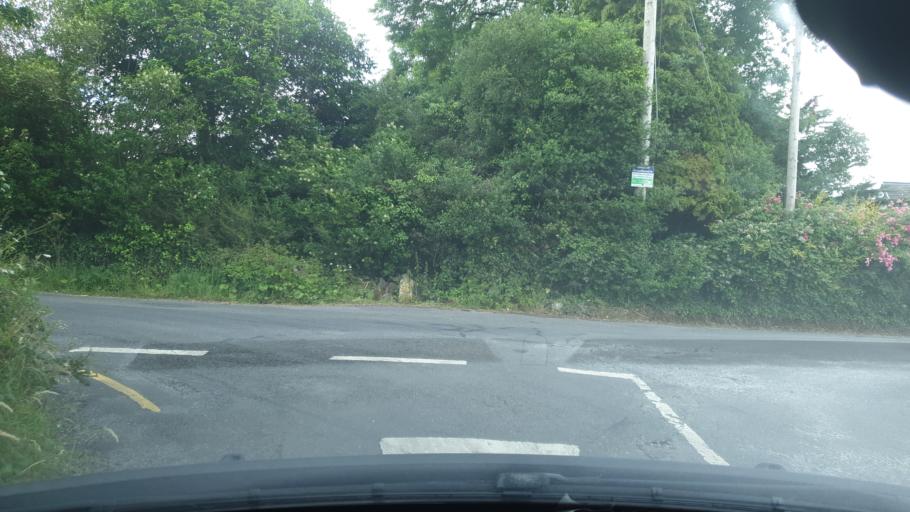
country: IE
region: Munster
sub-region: Ciarrai
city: Tralee
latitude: 52.2420
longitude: -9.6454
